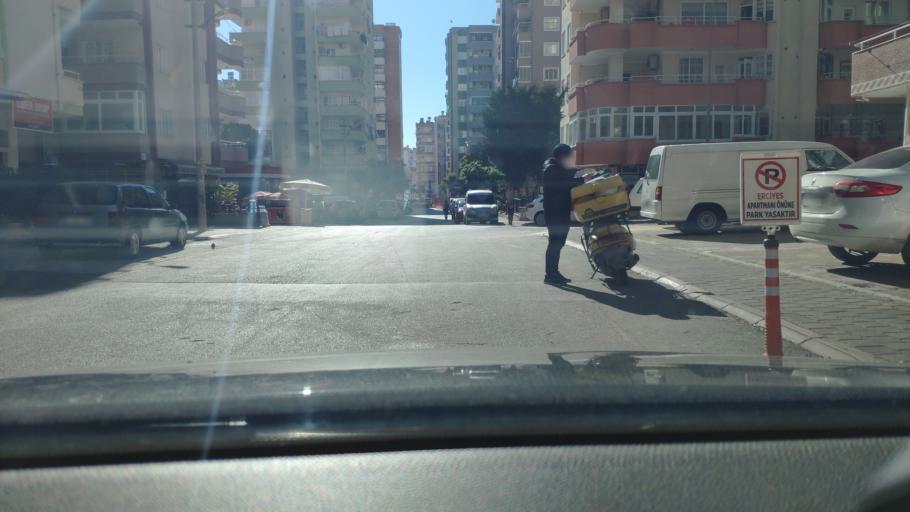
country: TR
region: Adana
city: Adana
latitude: 37.0540
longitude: 35.2814
